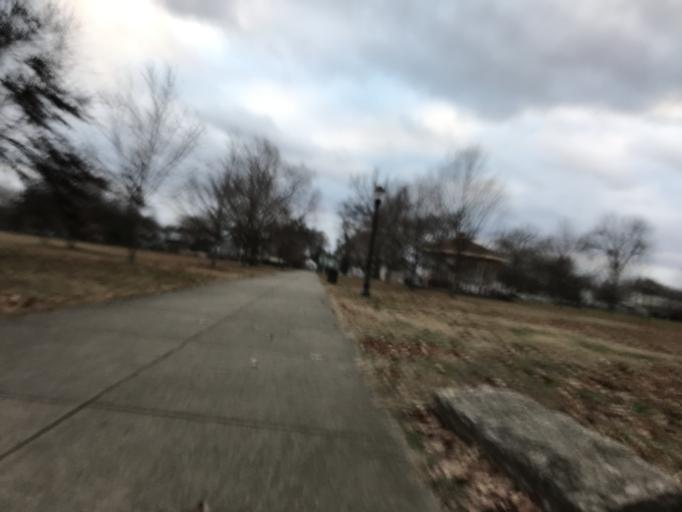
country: US
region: Kentucky
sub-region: Jefferson County
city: Louisville
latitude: 38.2333
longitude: -85.7454
